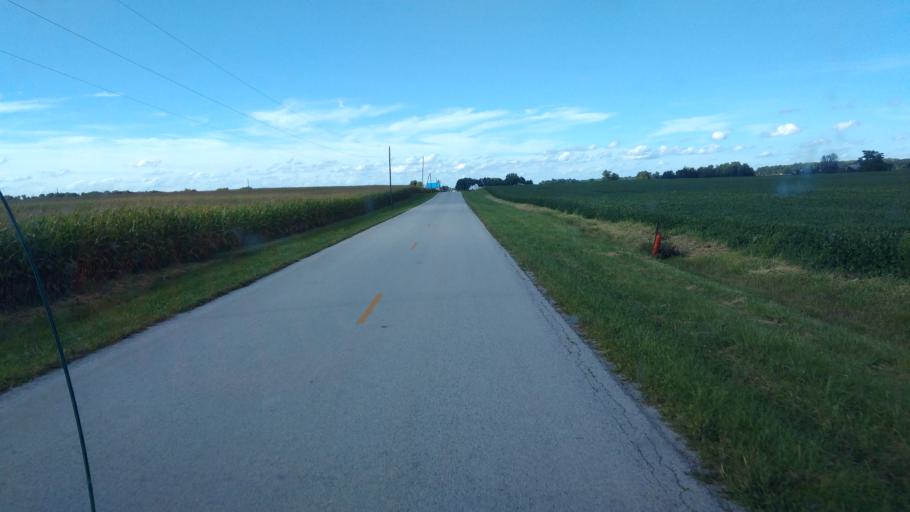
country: US
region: Ohio
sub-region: Hardin County
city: Kenton
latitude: 40.7370
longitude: -83.6907
